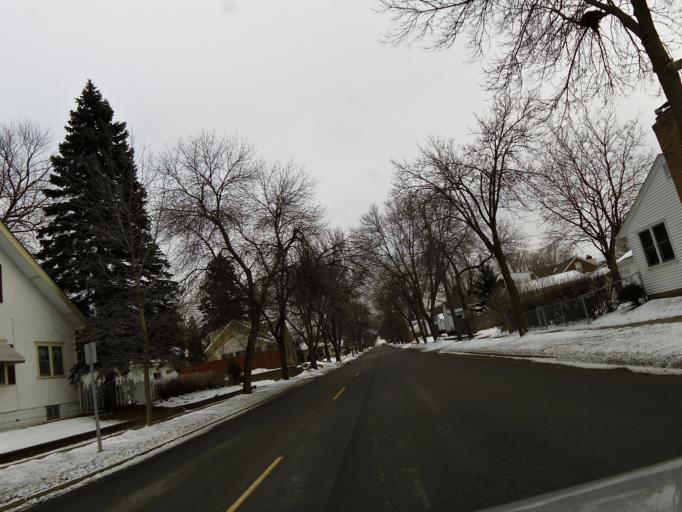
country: US
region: Minnesota
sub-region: Dakota County
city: Mendota Heights
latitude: 44.9234
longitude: -93.1925
